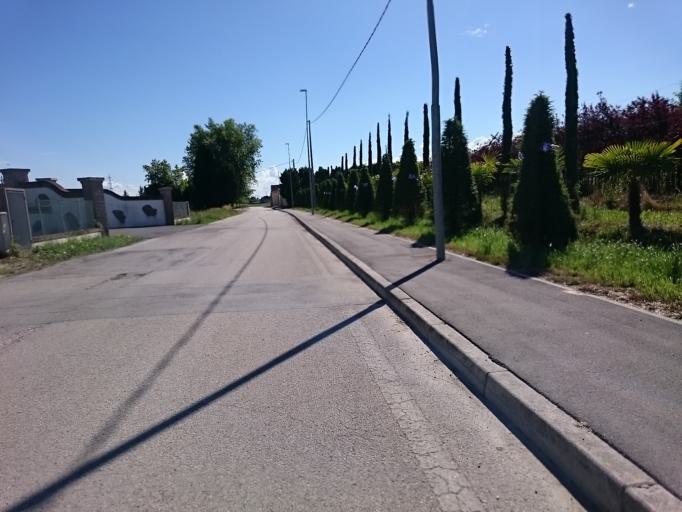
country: IT
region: Veneto
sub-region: Provincia di Padova
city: Saonara
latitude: 45.3680
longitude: 11.9820
